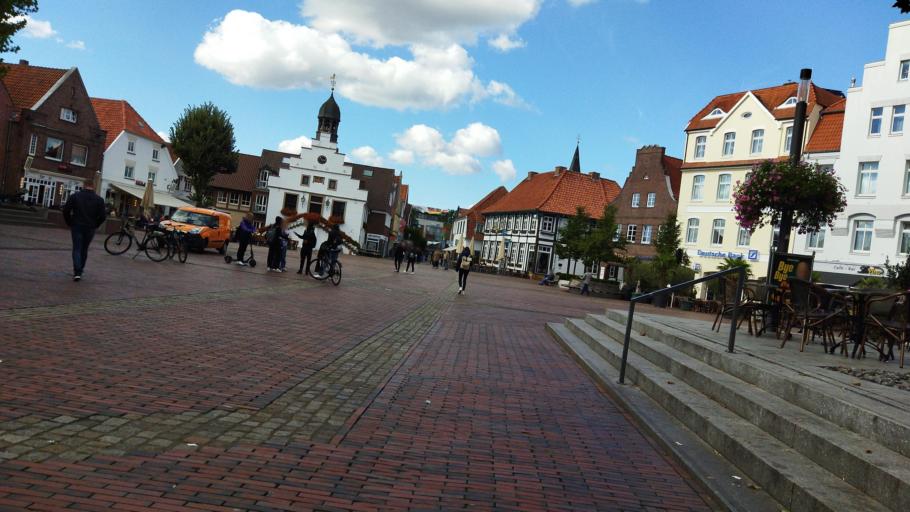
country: DE
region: Lower Saxony
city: Lingen
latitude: 52.5222
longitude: 7.3170
